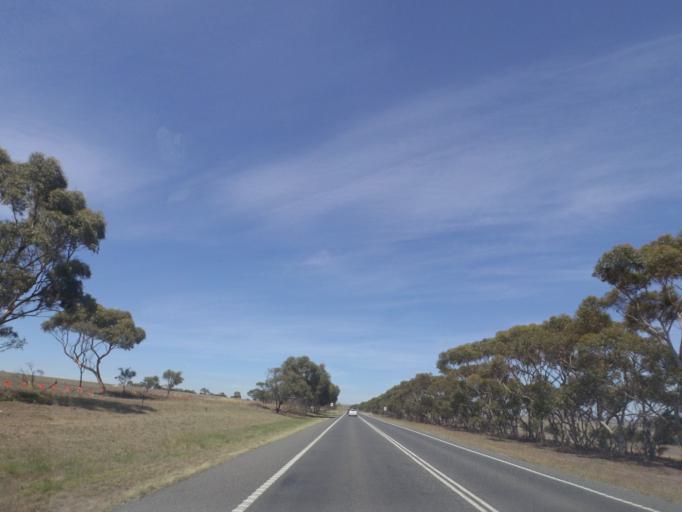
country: AU
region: Victoria
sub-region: Greater Geelong
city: Lara
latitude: -37.8896
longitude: 144.3712
